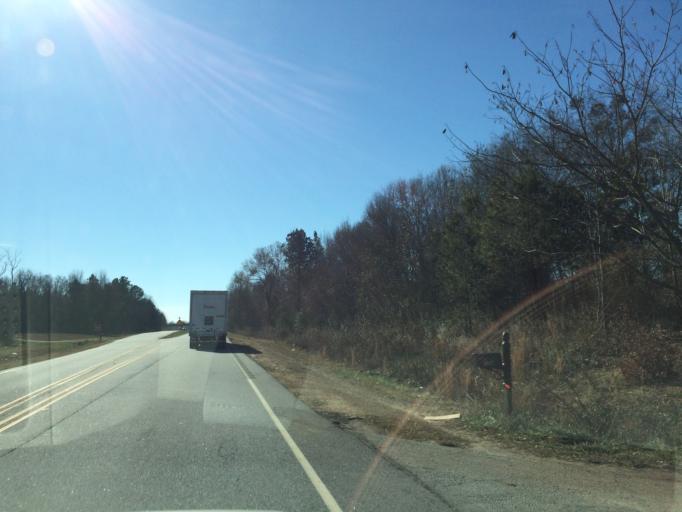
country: US
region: South Carolina
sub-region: Anderson County
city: Williamston
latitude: 34.6442
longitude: -82.5248
